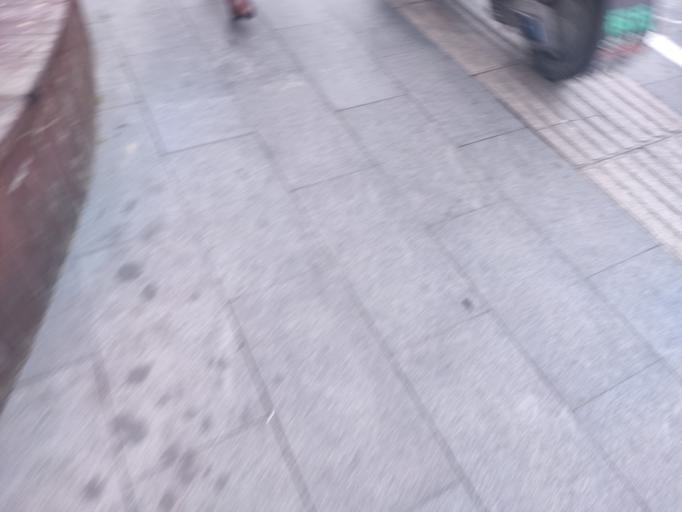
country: CN
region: Shanghai Shi
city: Huacao
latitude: 31.2081
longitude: 121.2924
